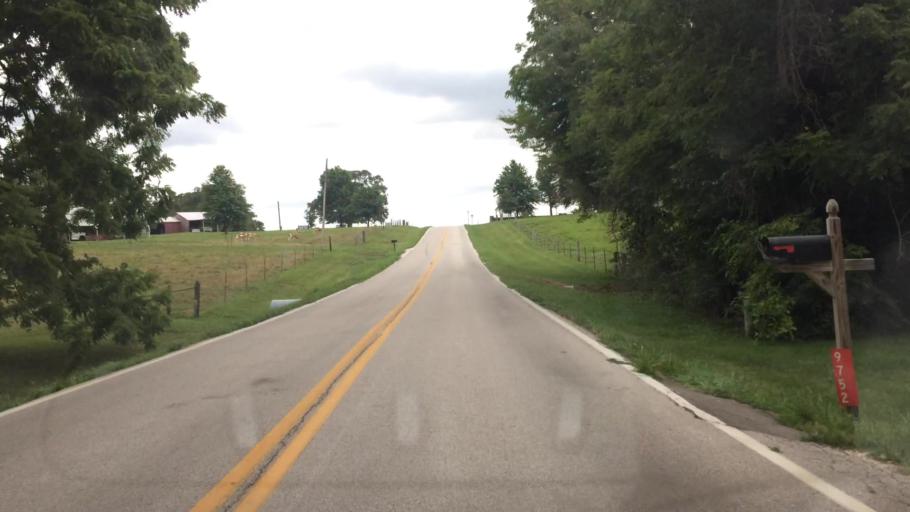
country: US
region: Missouri
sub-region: Greene County
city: Strafford
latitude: 37.3024
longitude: -93.0773
